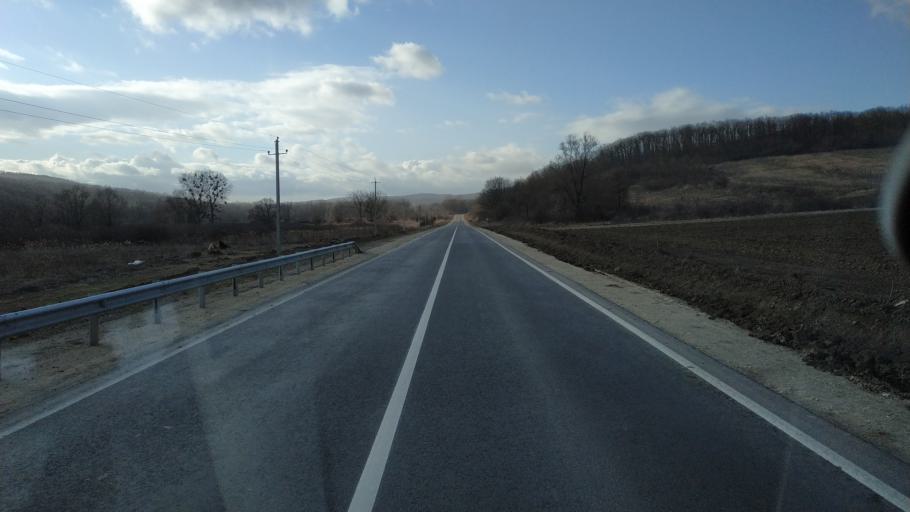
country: MD
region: Calarasi
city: Calarasi
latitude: 47.3005
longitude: 28.1503
